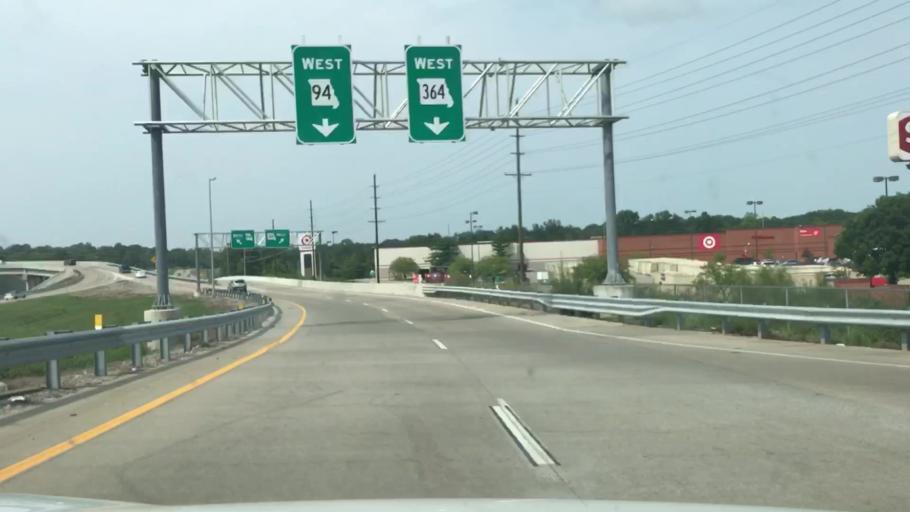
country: US
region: Missouri
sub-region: Saint Charles County
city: Cottleville
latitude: 38.7389
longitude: -90.6339
